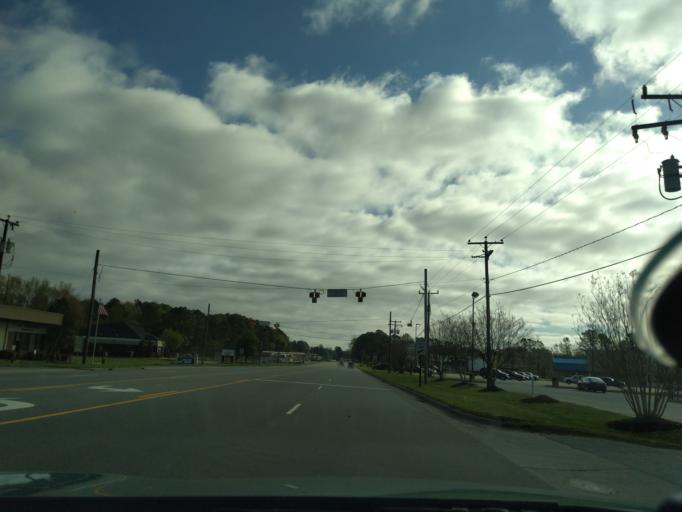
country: US
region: North Carolina
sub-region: Washington County
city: Plymouth
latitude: 35.8623
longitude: -76.7334
